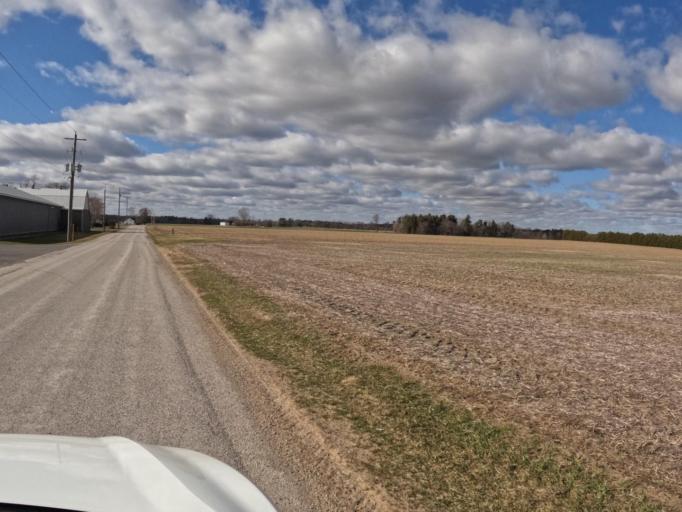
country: CA
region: Ontario
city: Norfolk County
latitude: 42.7461
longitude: -80.3828
